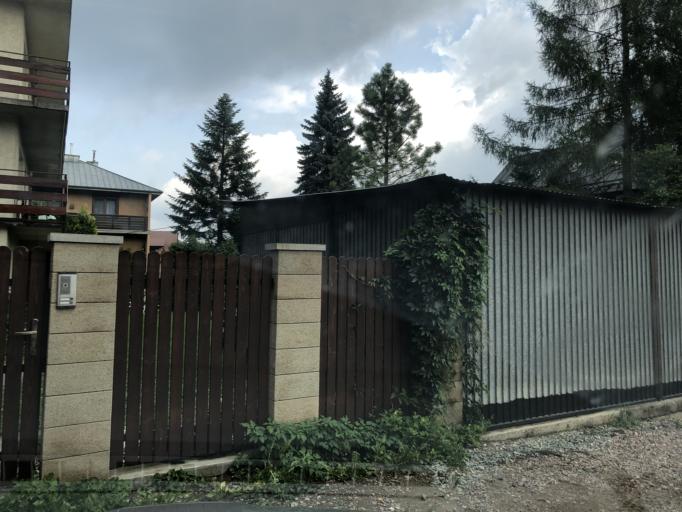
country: PL
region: Lesser Poland Voivodeship
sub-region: Powiat krakowski
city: Libertow
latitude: 50.0025
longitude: 19.9269
